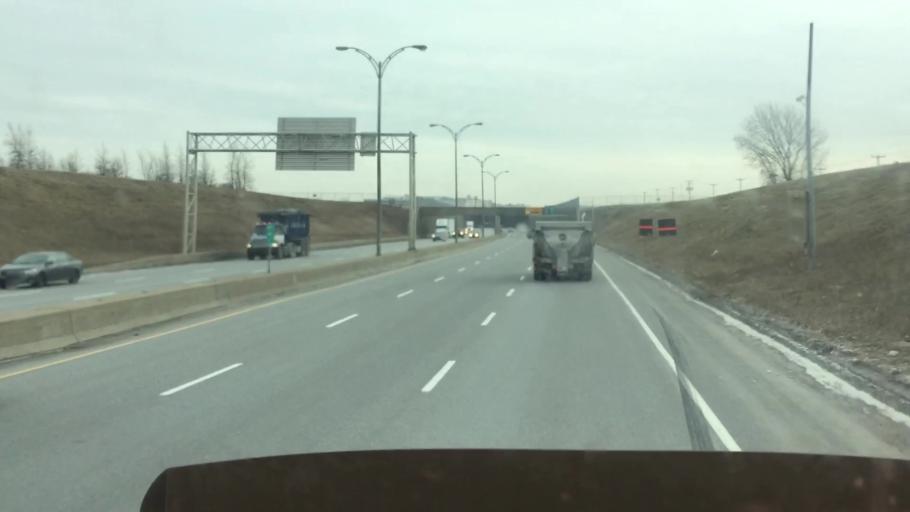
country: CA
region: Quebec
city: Dorval
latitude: 45.4816
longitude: -73.7228
